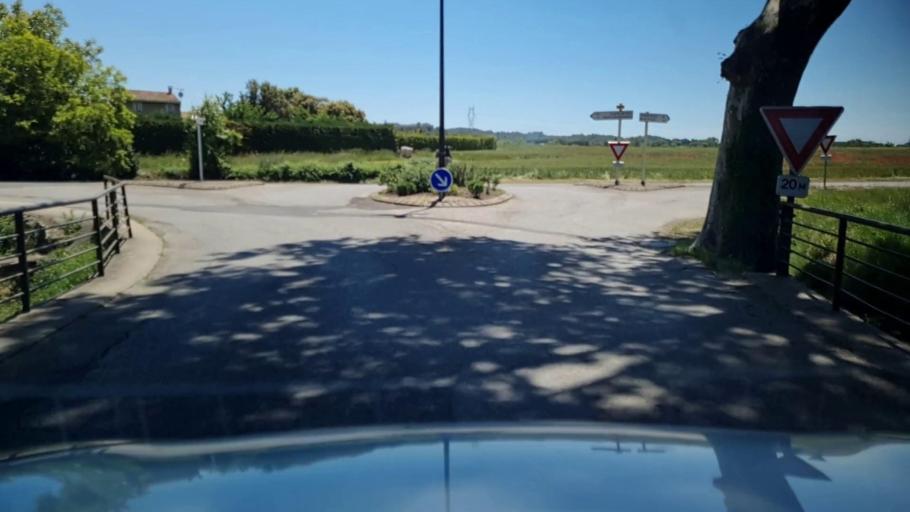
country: FR
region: Languedoc-Roussillon
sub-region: Departement du Gard
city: Saint-Mamert-du-Gard
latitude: 43.8850
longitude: 4.1893
